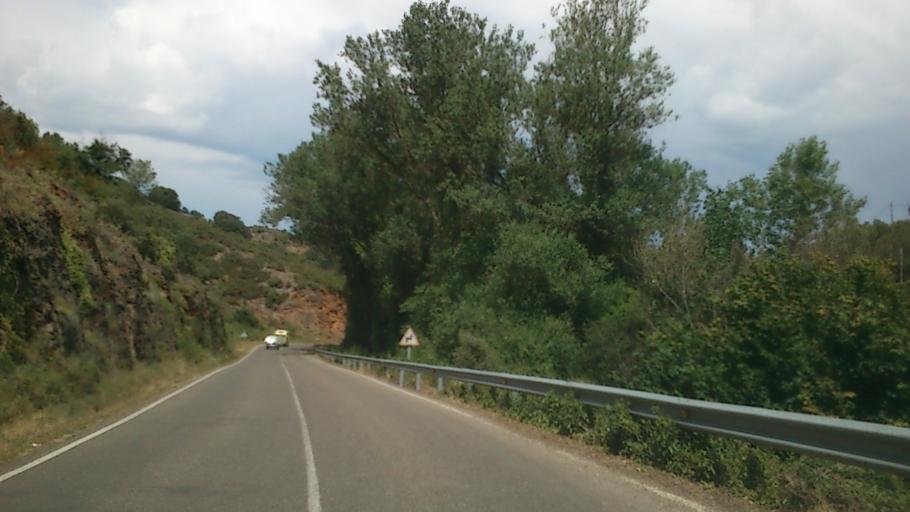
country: ES
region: Castille and Leon
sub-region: Provincia de Burgos
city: Frias
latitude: 42.7567
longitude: -3.2962
